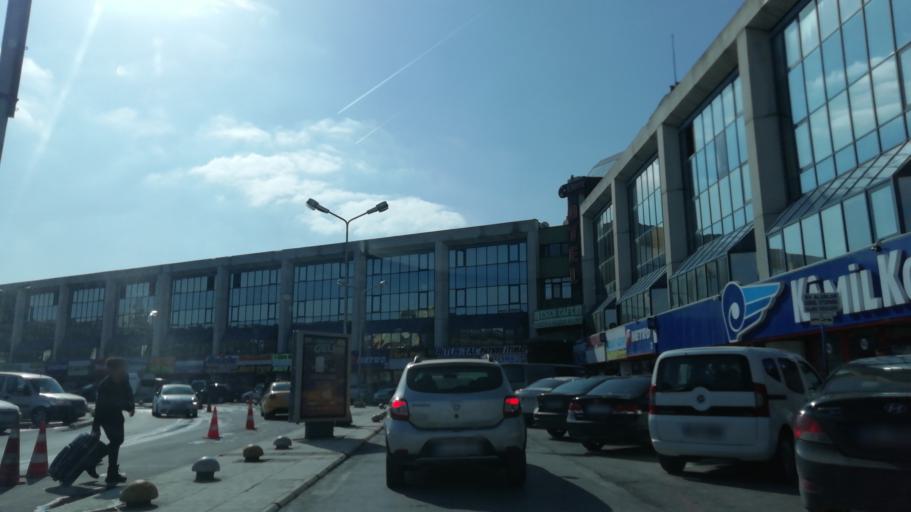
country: TR
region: Istanbul
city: Esenler
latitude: 41.0398
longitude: 28.8935
